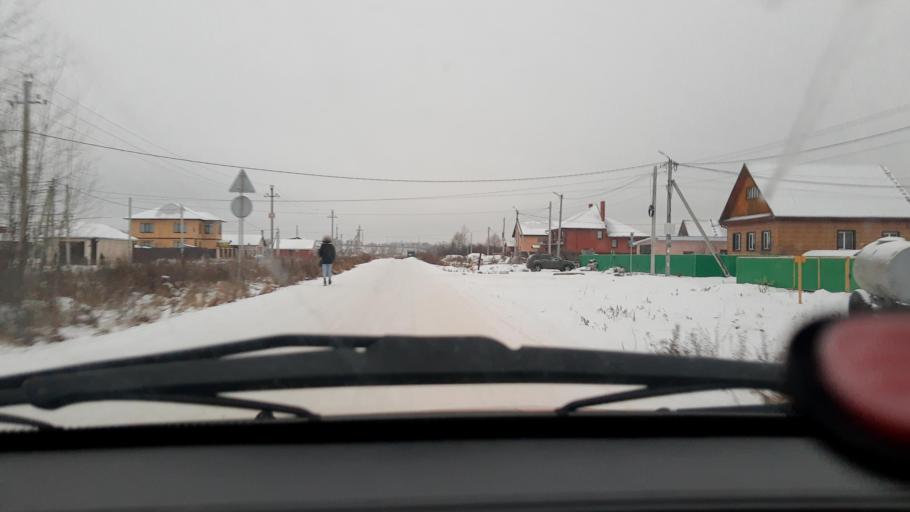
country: RU
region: Bashkortostan
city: Mikhaylovka
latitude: 54.7899
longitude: 55.8243
